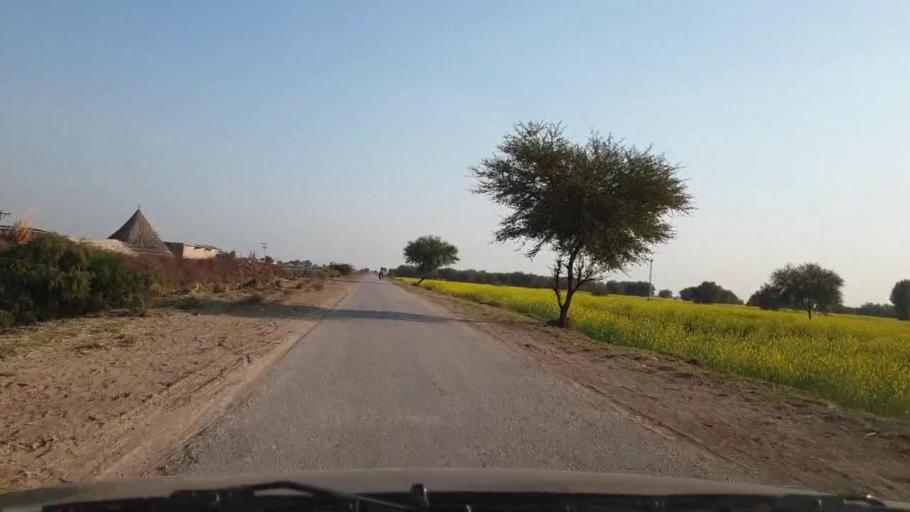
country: PK
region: Sindh
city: Jhol
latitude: 25.9473
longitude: 68.9047
